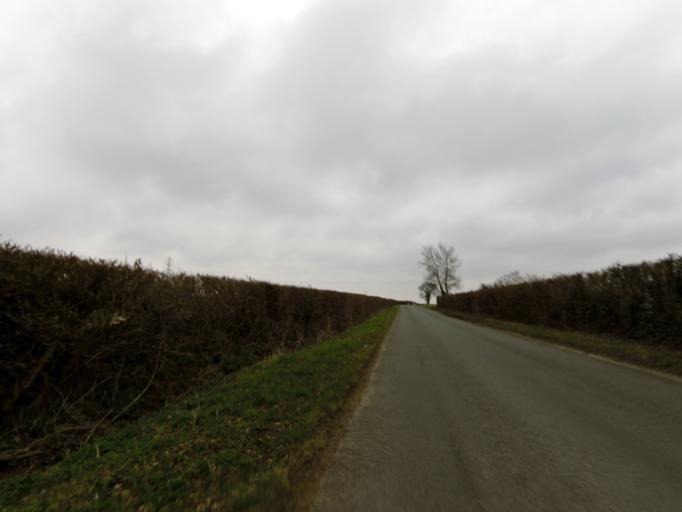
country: GB
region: England
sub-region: Suffolk
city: Framlingham
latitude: 52.2047
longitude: 1.3300
